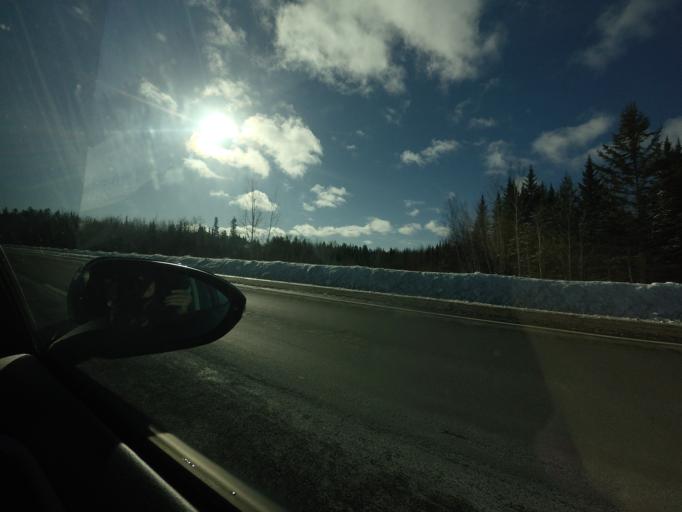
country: CA
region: New Brunswick
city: Fredericton
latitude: 45.8774
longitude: -66.6331
